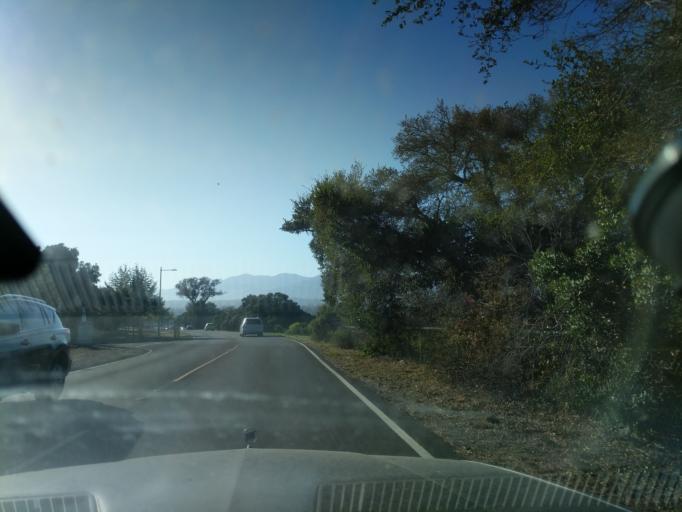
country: US
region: California
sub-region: Santa Barbara County
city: Isla Vista
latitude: 34.4202
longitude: -119.8496
